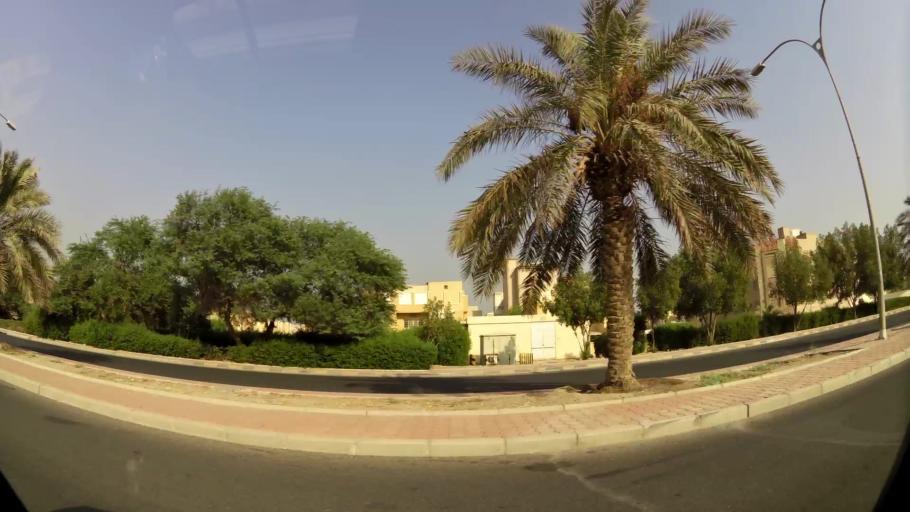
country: KW
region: Al Ahmadi
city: Ar Riqqah
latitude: 29.1300
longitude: 48.1037
